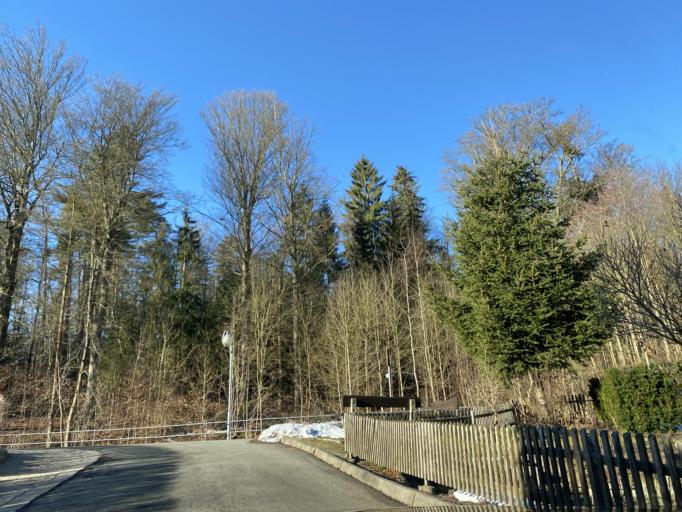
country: DE
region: Saxony
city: Thermalbad Wiesenbad
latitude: 50.6212
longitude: 13.0409
